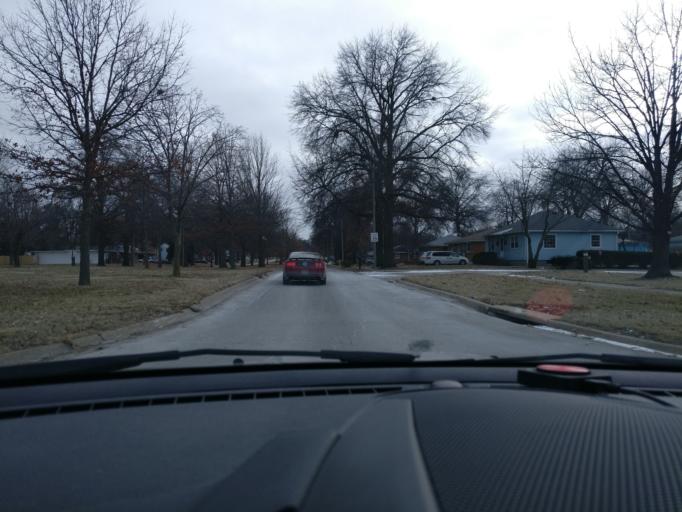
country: US
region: Nebraska
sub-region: Lancaster County
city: Lincoln
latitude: 40.8485
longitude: -96.6402
